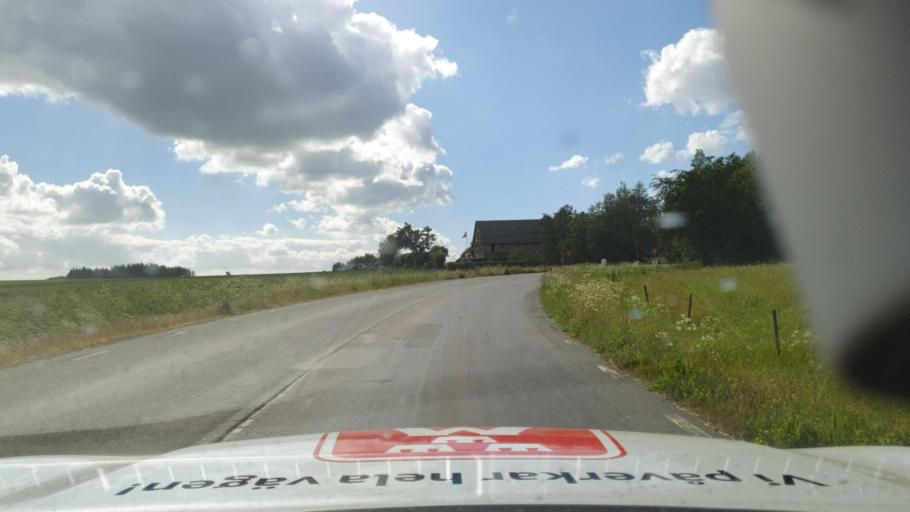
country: SE
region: Skane
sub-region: Simrishamns Kommun
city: Simrishamn
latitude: 55.5528
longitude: 14.3179
